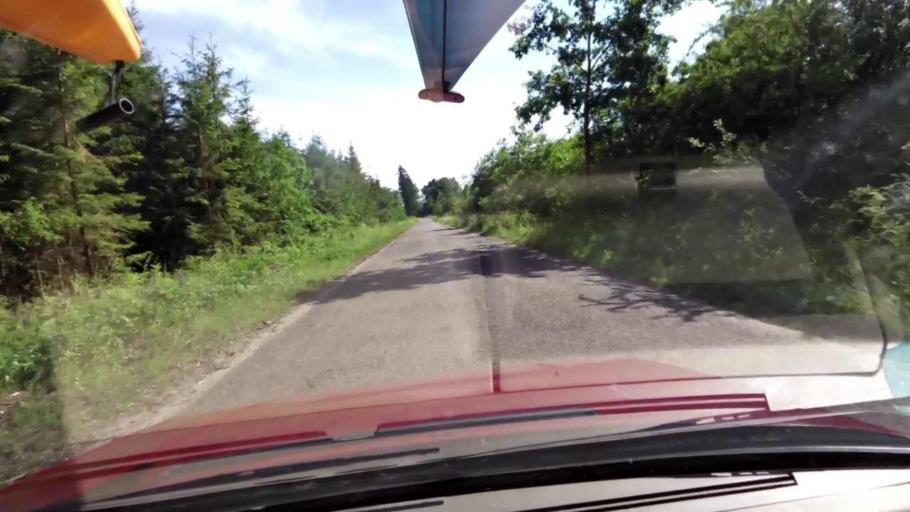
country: PL
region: Pomeranian Voivodeship
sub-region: Powiat slupski
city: Kepice
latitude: 54.1840
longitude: 16.8887
